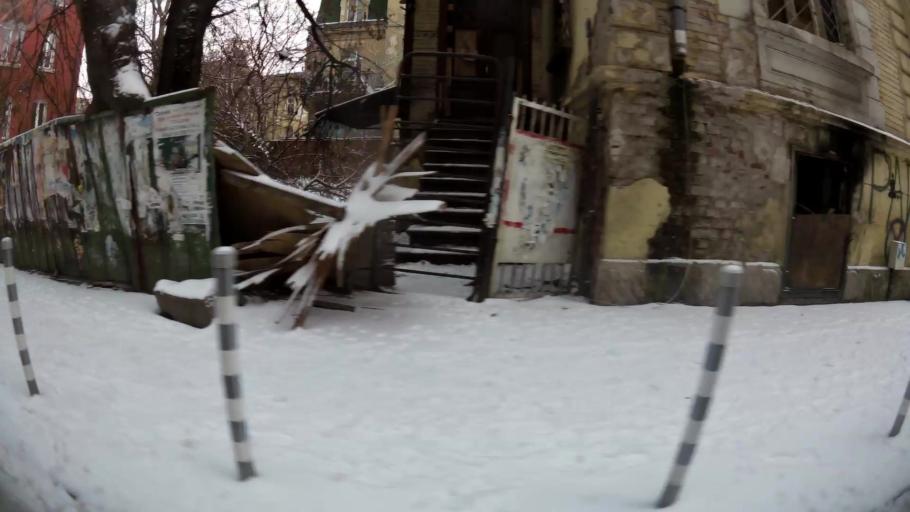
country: BG
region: Sofia-Capital
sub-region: Stolichna Obshtina
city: Sofia
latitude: 42.7016
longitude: 23.3281
